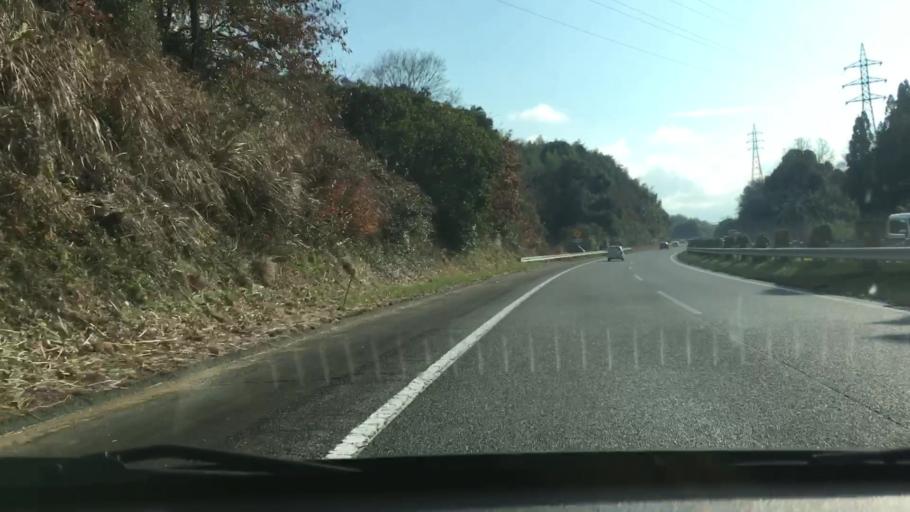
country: JP
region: Kumamoto
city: Matsubase
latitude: 32.6351
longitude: 130.7101
